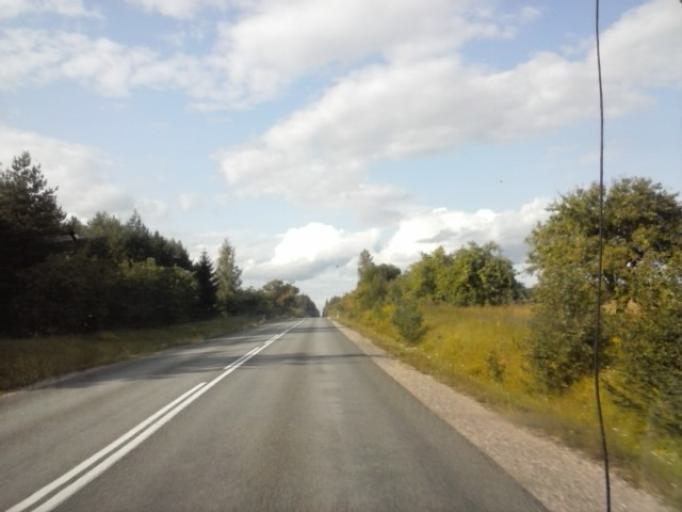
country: LV
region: Valmieras Rajons
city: Valmiera
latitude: 57.4803
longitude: 25.4082
